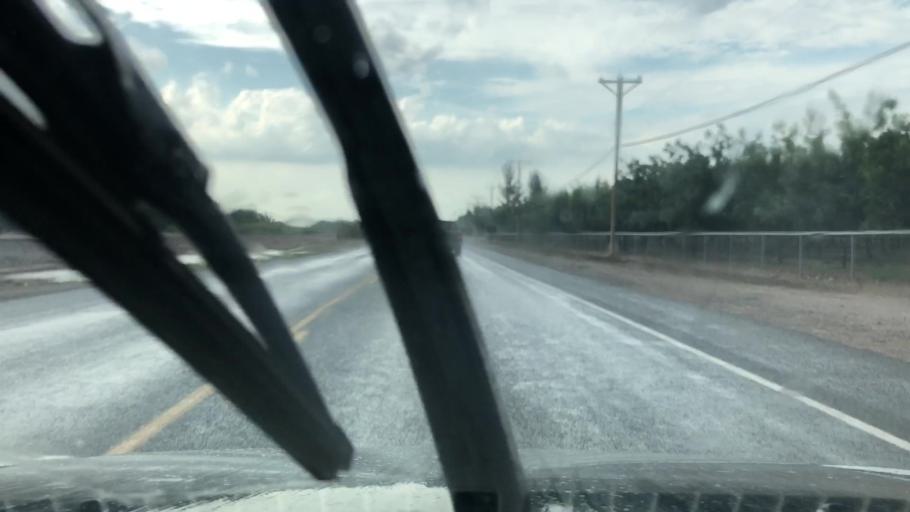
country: US
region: New Mexico
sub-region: Dona Ana County
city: Mesquite
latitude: 32.1928
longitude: -106.7143
